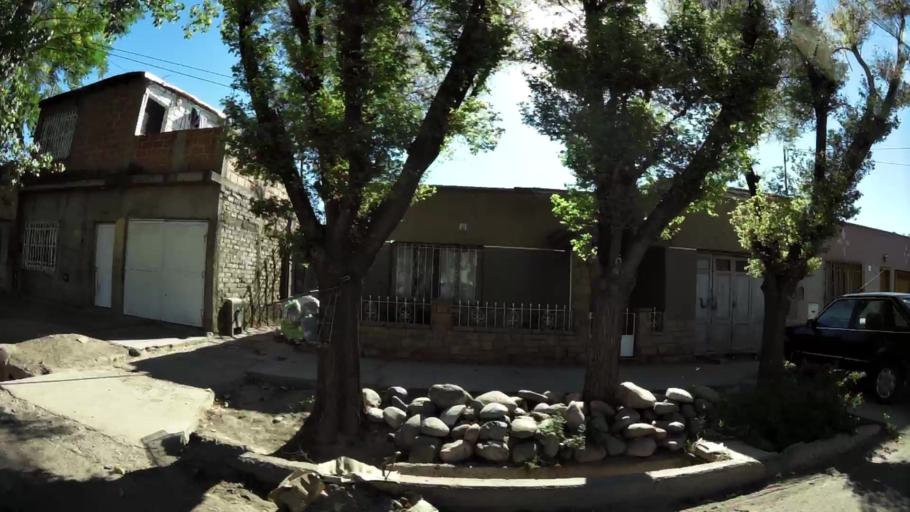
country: AR
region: Mendoza
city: Las Heras
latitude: -32.8467
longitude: -68.8311
